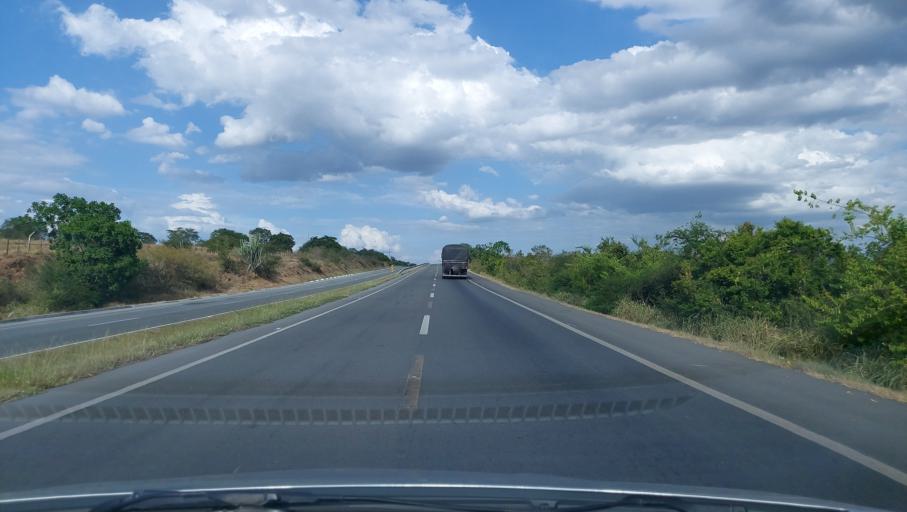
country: BR
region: Bahia
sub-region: Castro Alves
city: Castro Alves
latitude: -12.5659
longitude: -39.4840
